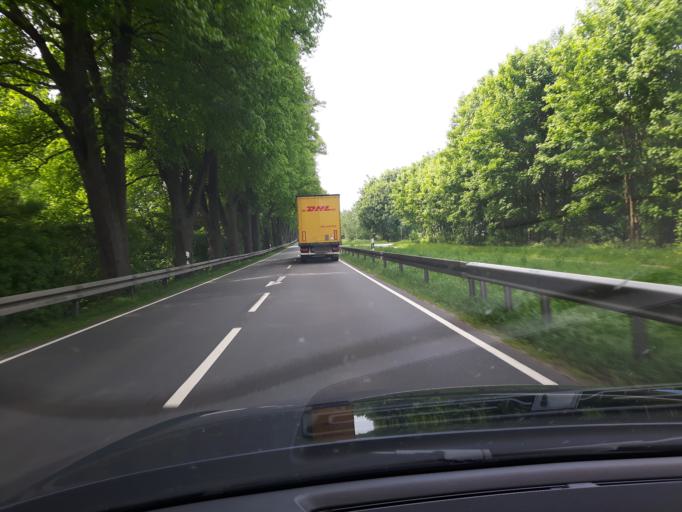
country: DE
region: Mecklenburg-Vorpommern
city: Selmsdorf
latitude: 53.8687
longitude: 10.8967
